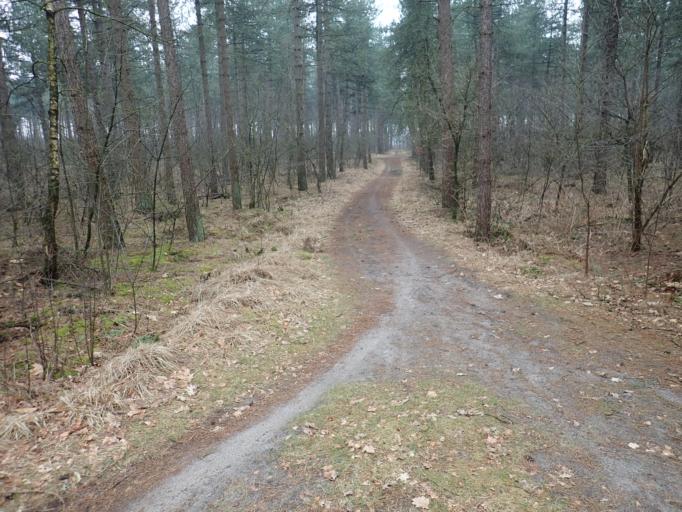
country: BE
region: Flanders
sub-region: Provincie Antwerpen
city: Essen
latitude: 51.4808
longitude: 4.5224
